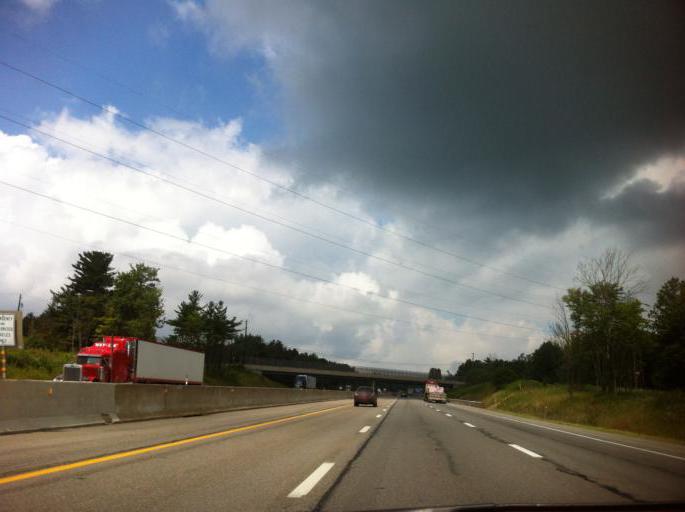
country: US
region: Ohio
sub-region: Summit County
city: Richfield
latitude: 41.2795
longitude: -81.6466
